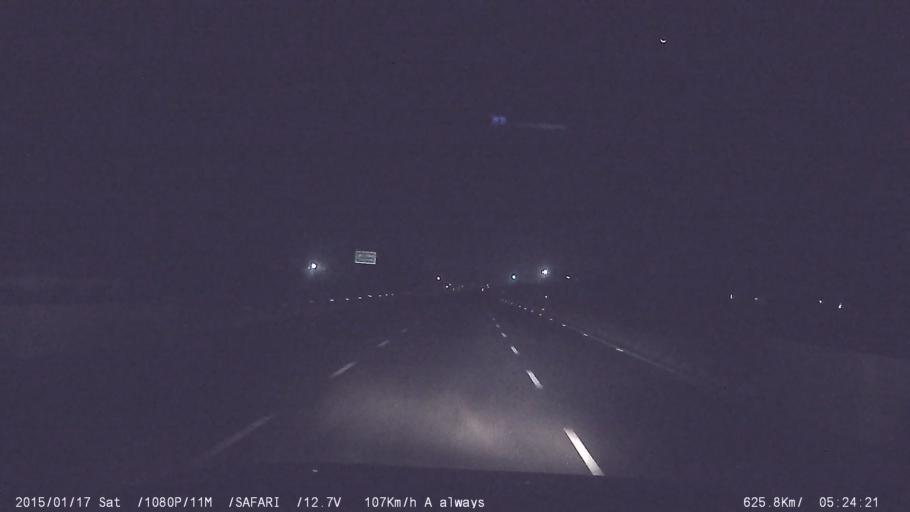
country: IN
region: Tamil Nadu
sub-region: Vellore
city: Katpadi
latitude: 12.9476
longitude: 79.2189
